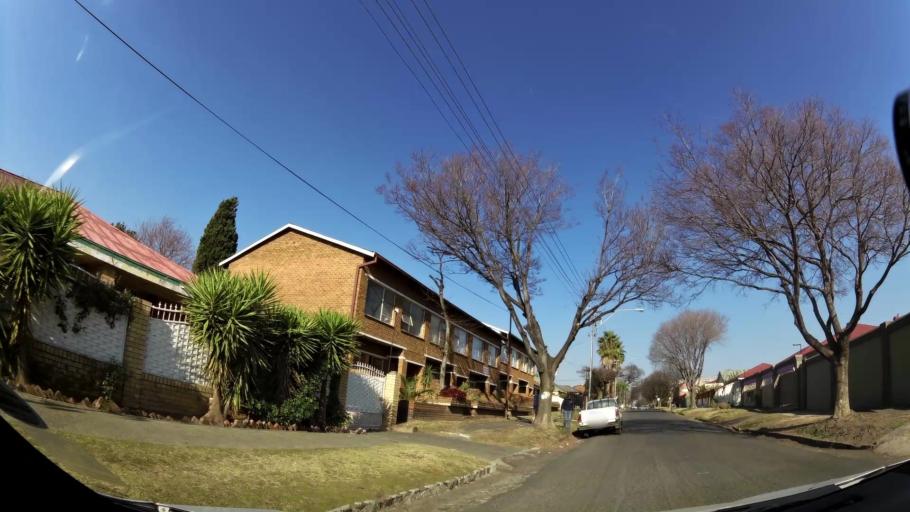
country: ZA
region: Gauteng
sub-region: City of Johannesburg Metropolitan Municipality
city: Johannesburg
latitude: -26.2348
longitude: 28.0218
